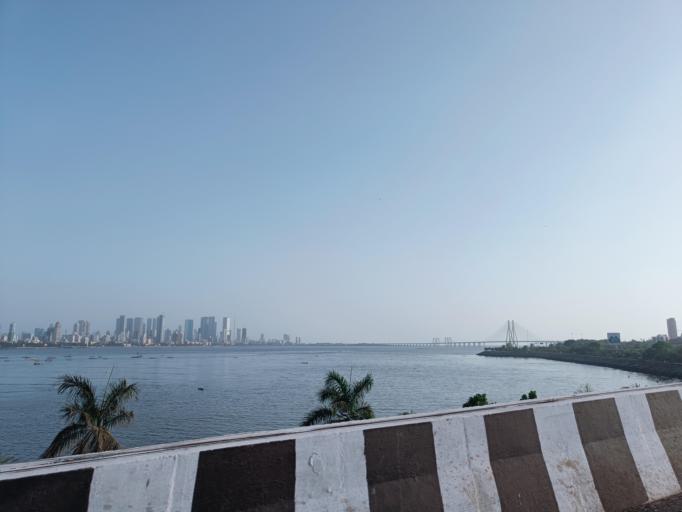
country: IN
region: Maharashtra
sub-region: Mumbai Suburban
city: Mumbai
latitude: 19.0516
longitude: 72.8363
